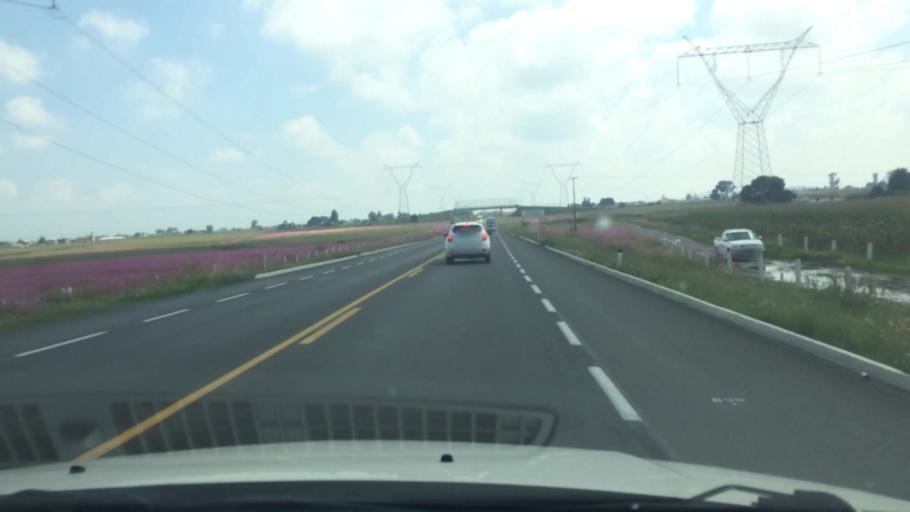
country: MX
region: Mexico
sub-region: Toluca
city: Sebastian Lerdo de Tejada
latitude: 19.3876
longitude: -99.7351
